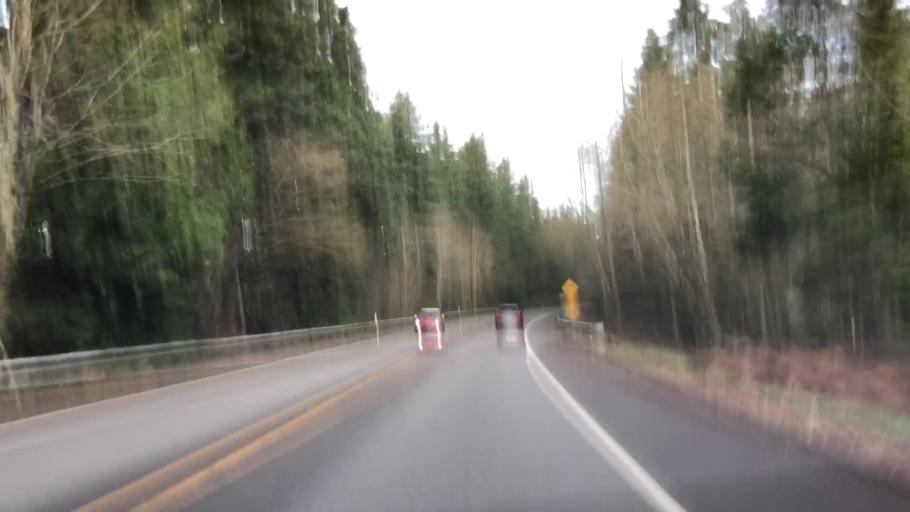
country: US
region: Washington
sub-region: Kitsap County
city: Bainbridge Island
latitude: 47.6469
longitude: -122.5222
